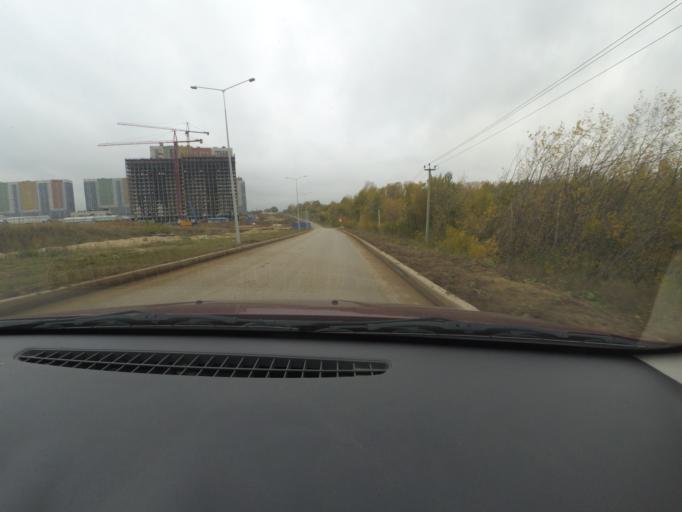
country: RU
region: Nizjnij Novgorod
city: Afonino
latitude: 56.2481
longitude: 44.0528
